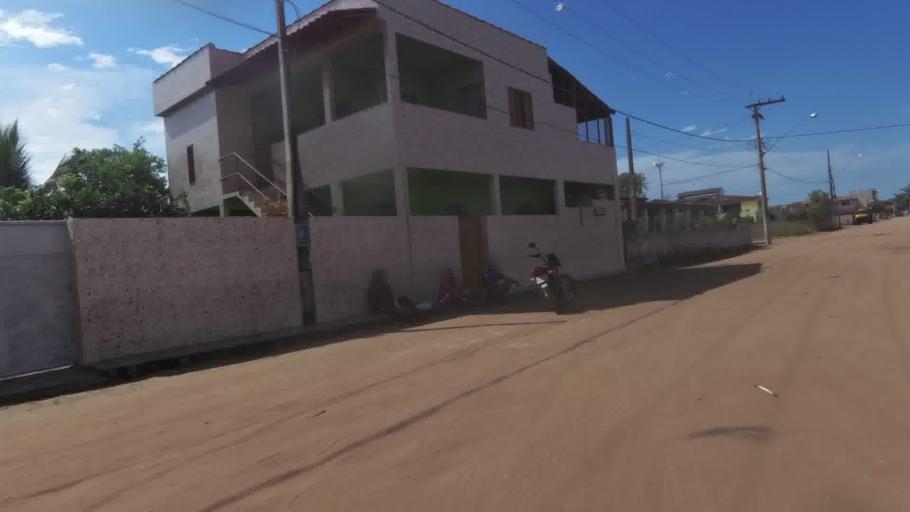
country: BR
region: Espirito Santo
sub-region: Piuma
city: Piuma
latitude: -20.8484
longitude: -40.7521
